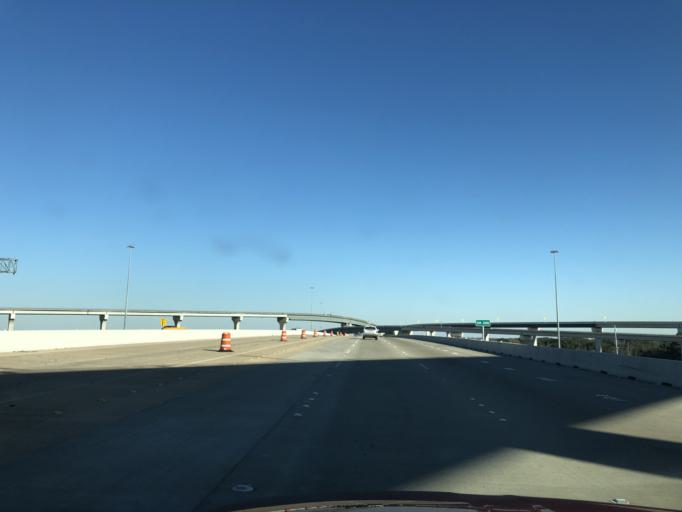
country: US
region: Texas
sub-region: Brazoria County
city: Brookside Village
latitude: 29.5975
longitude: -95.3890
